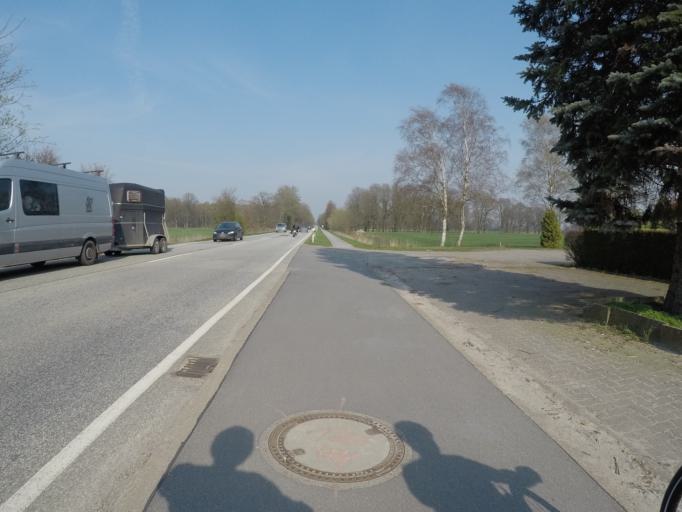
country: DE
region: Schleswig-Holstein
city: Gross Niendorf
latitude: 53.8365
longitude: 10.2216
